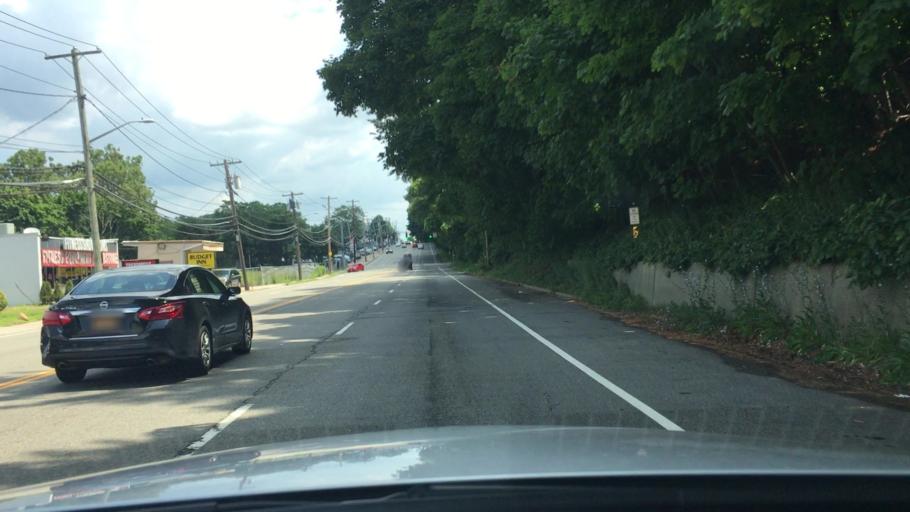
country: US
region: New York
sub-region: Suffolk County
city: West Hills
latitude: 40.8276
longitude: -73.4360
